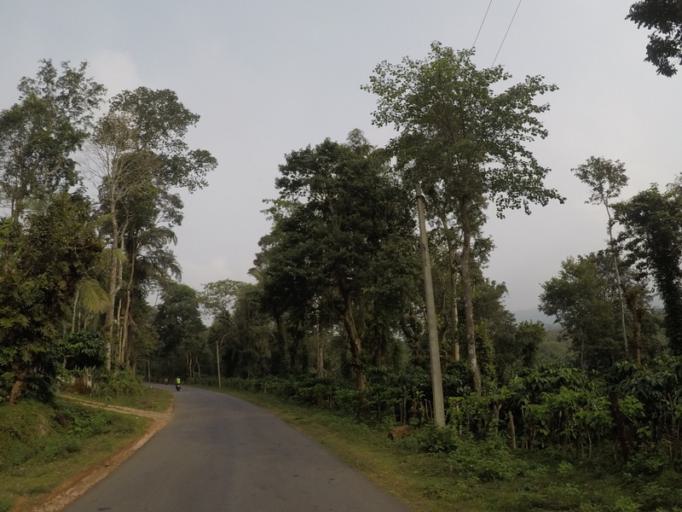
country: IN
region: Karnataka
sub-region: Chikmagalur
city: Chikmagalur
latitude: 13.3482
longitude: 75.5419
